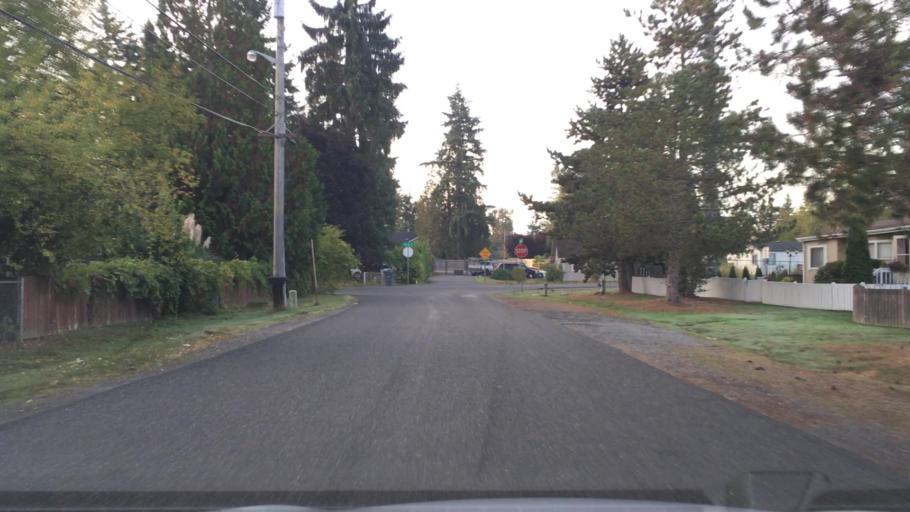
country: US
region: Washington
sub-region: Pierce County
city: Midland
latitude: 47.1809
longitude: -122.4024
